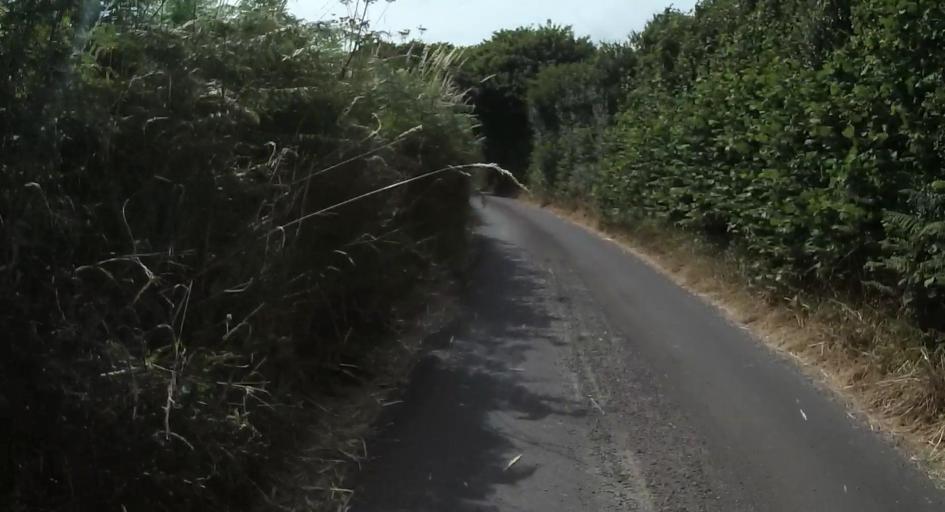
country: GB
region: England
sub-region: Dorset
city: Swanage
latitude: 50.6353
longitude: -2.0331
